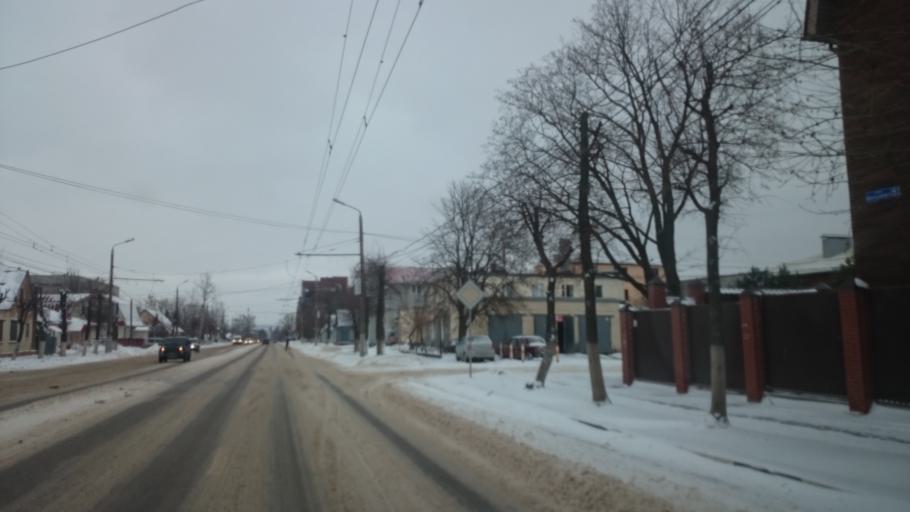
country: RU
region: Tula
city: Mendeleyevskiy
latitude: 54.1792
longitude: 37.5738
